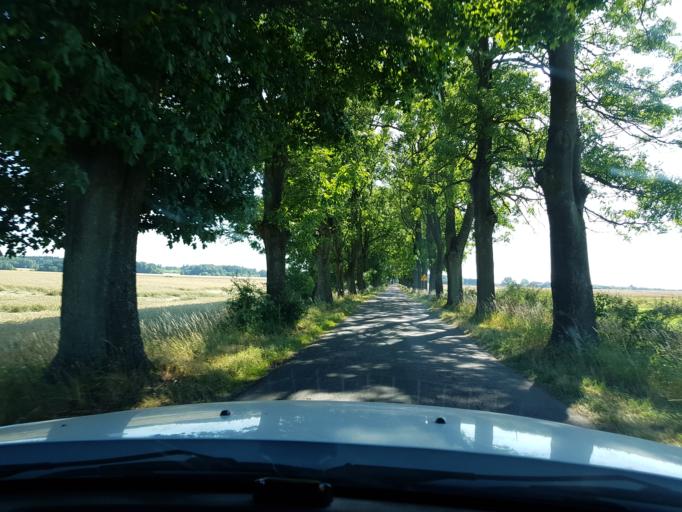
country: PL
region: West Pomeranian Voivodeship
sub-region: Powiat swidwinski
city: Slawoborze
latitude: 53.8538
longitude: 15.7259
